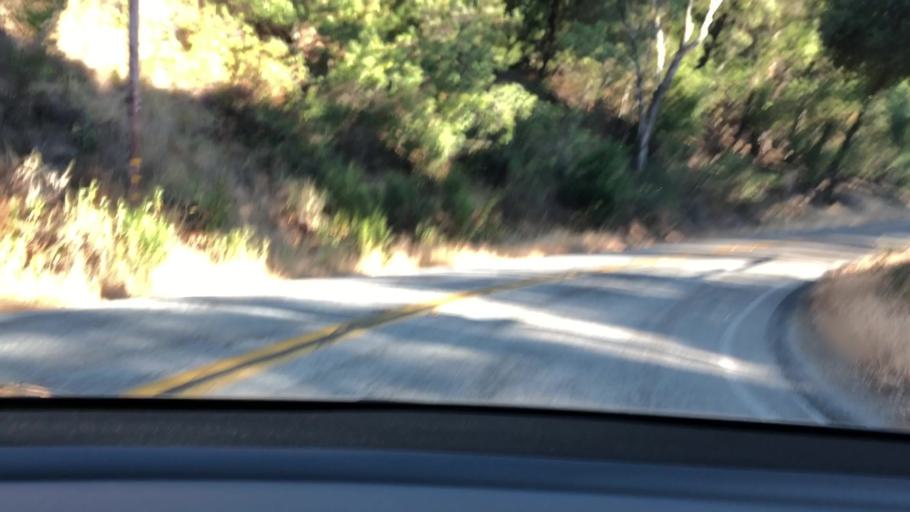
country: US
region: California
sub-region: Santa Clara County
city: Saratoga
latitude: 37.2808
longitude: -122.0727
